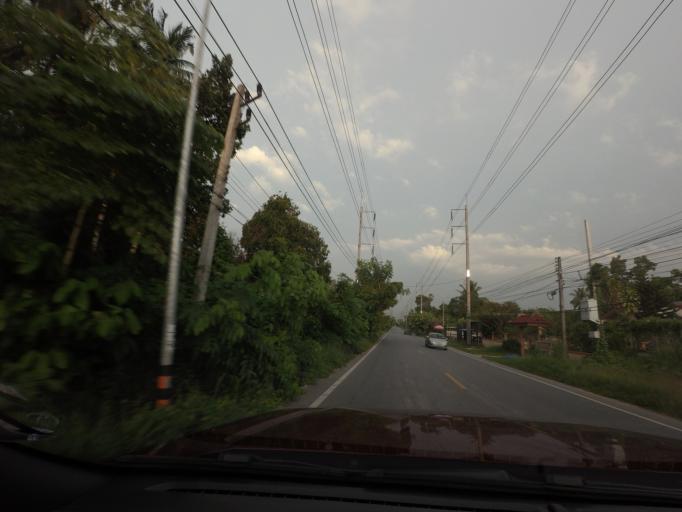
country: TH
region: Yala
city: Yala
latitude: 6.5728
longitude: 101.2018
